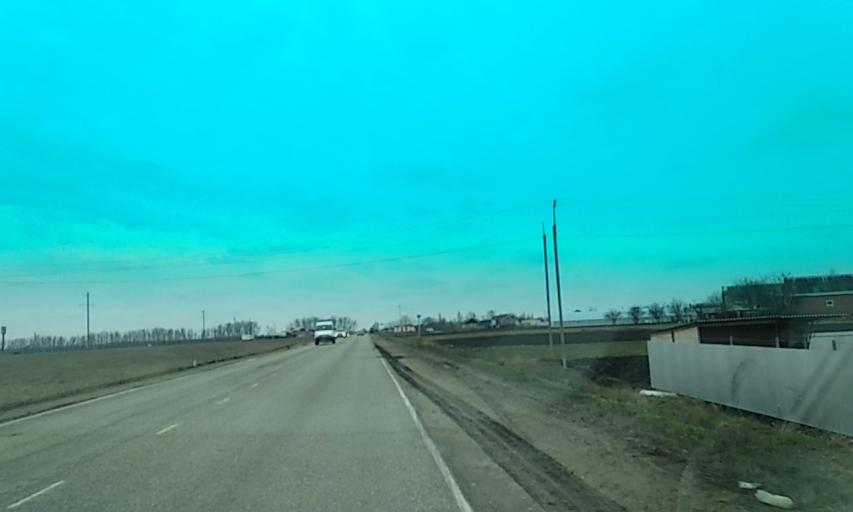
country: RU
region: Krasnodarskiy
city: Ust'-Labinsk
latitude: 45.3696
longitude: 39.7057
